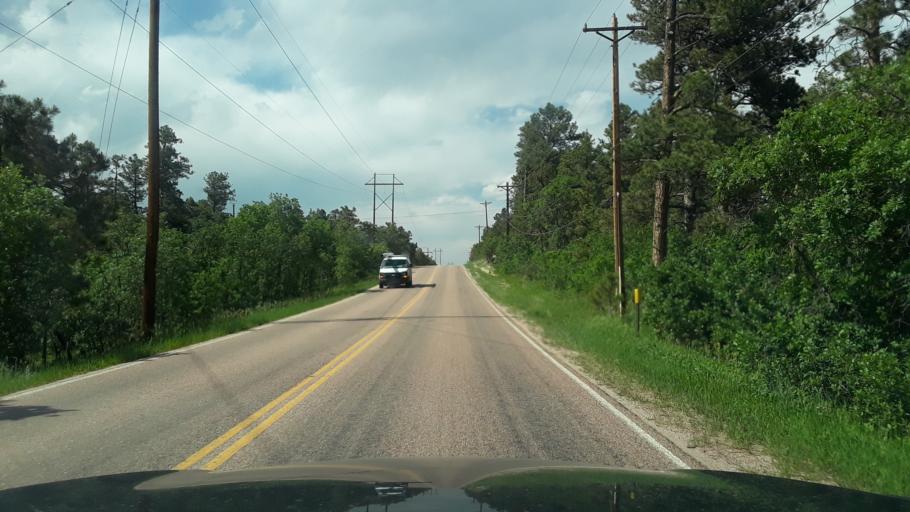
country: US
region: Colorado
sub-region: El Paso County
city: Gleneagle
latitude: 39.0385
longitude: -104.7848
